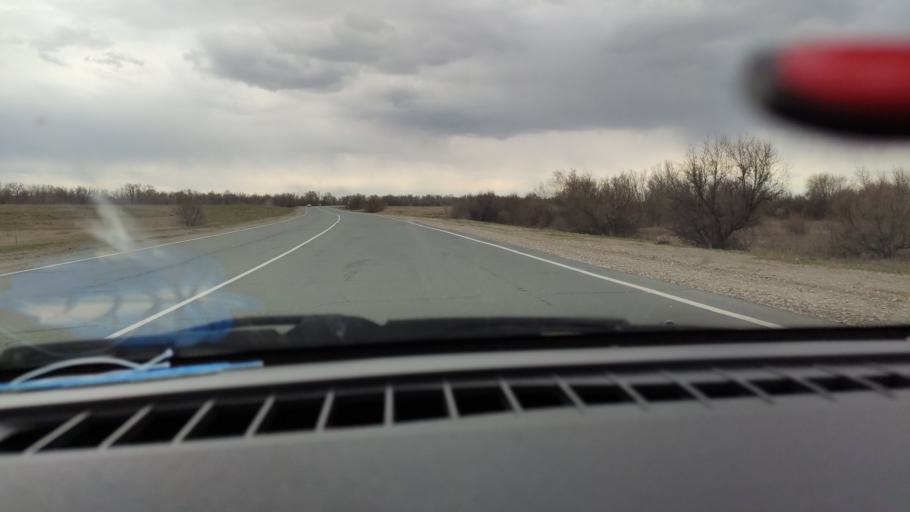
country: RU
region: Saratov
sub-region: Saratovskiy Rayon
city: Saratov
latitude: 51.7167
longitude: 46.0257
